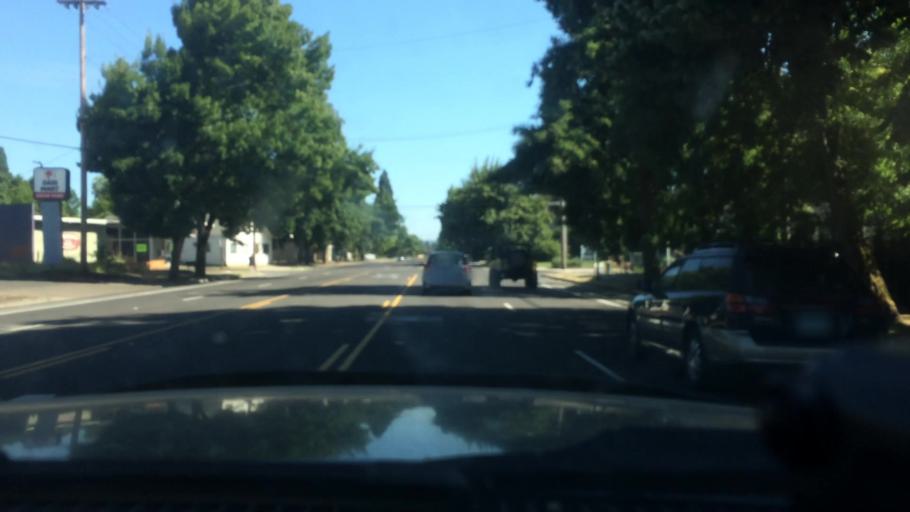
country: US
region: Oregon
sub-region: Lane County
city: Eugene
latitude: 44.0868
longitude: -123.1244
